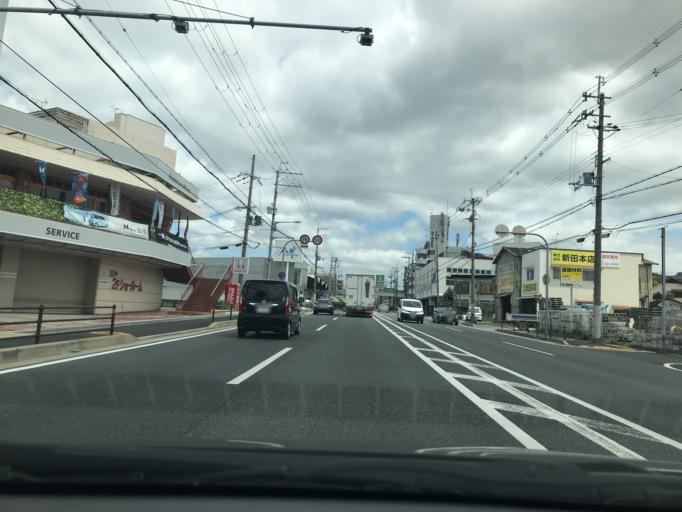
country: JP
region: Osaka
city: Mino
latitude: 34.8169
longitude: 135.4651
